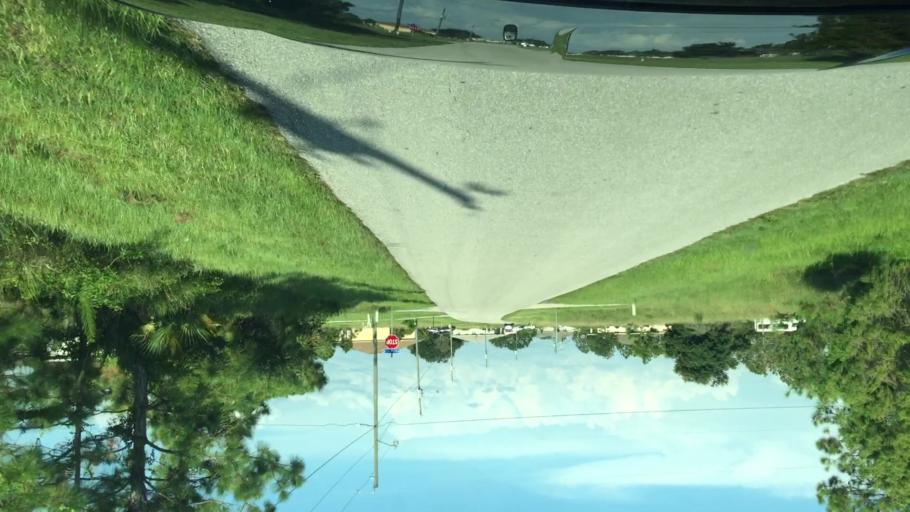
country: US
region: Florida
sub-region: Lee County
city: Gateway
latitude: 26.5896
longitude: -81.7186
